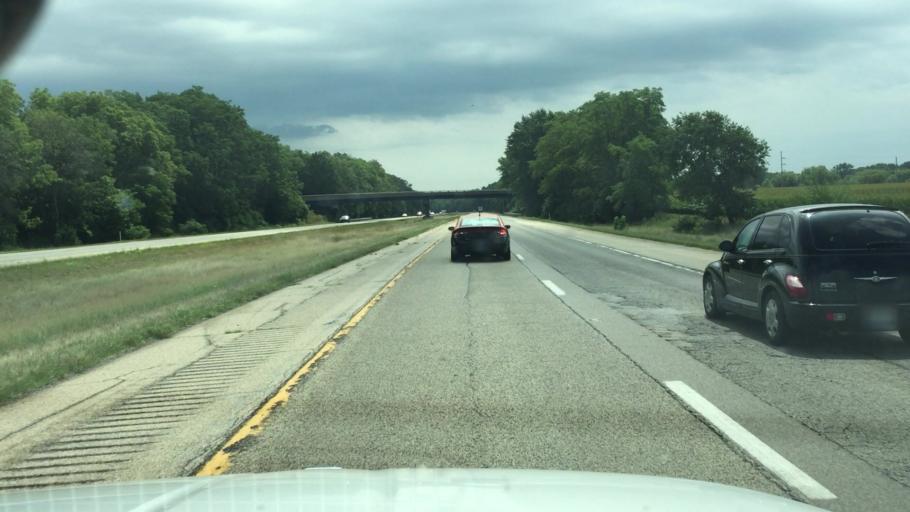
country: US
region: Illinois
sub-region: Peoria County
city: Hanna City
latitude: 40.8096
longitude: -89.8349
